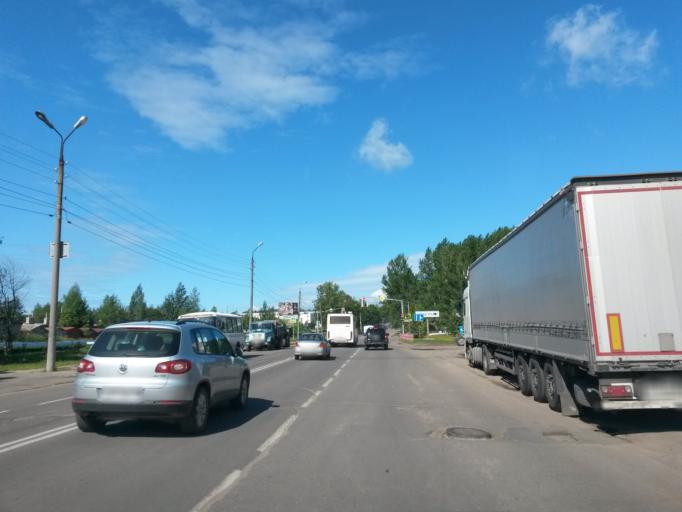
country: RU
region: Jaroslavl
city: Yaroslavl
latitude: 57.5703
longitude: 39.8603
